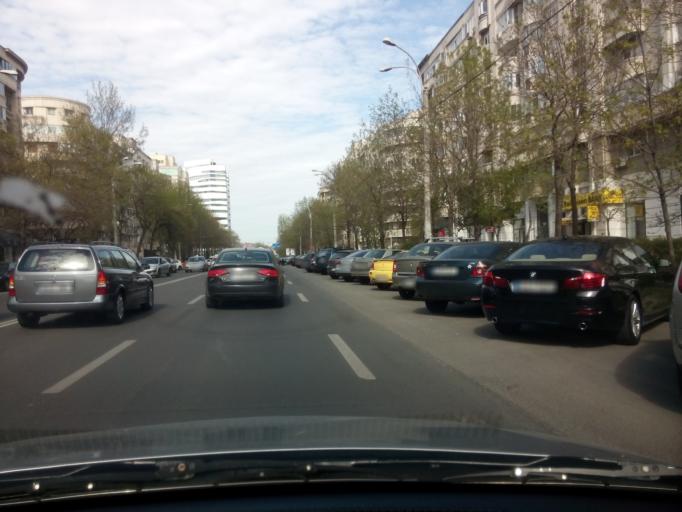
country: RO
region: Bucuresti
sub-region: Municipiul Bucuresti
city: Bucharest
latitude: 44.4295
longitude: 26.1343
